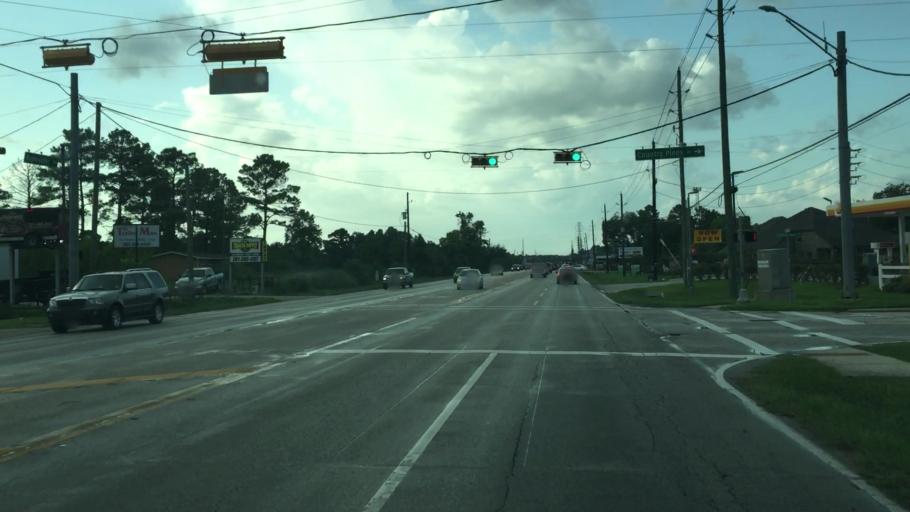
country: US
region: Texas
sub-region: Harris County
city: Spring
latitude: 30.0458
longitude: -95.4908
